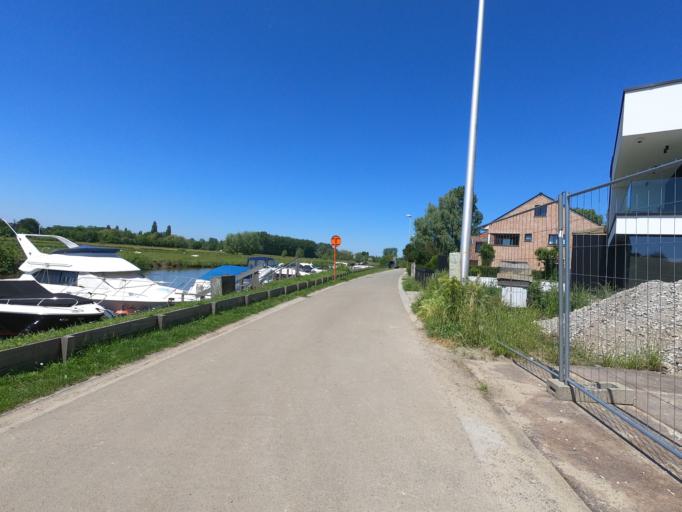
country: BE
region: Flanders
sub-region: Provincie Oost-Vlaanderen
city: Sint-Martens-Latem
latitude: 51.0399
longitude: 3.6612
